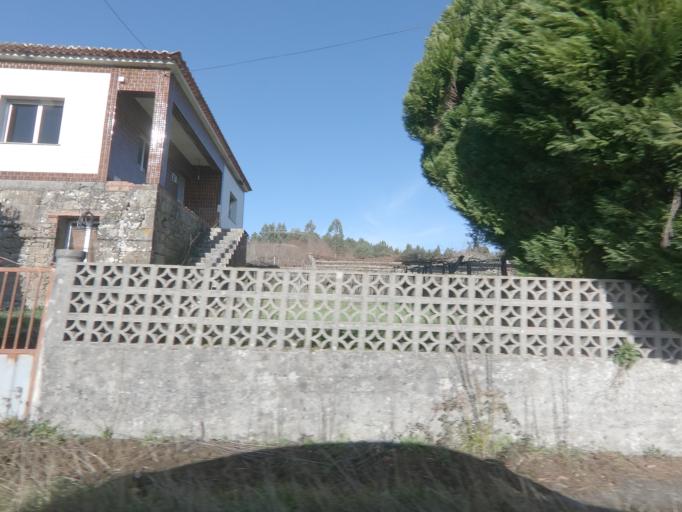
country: ES
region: Galicia
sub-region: Provincia da Coruna
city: Ribeira
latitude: 42.7157
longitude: -8.4374
